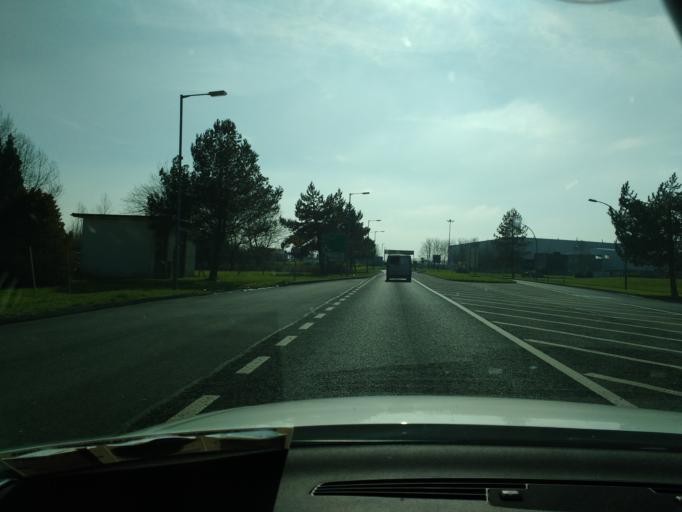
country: IE
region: Munster
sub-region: An Clar
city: Shannon
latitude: 52.6976
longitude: -8.9006
